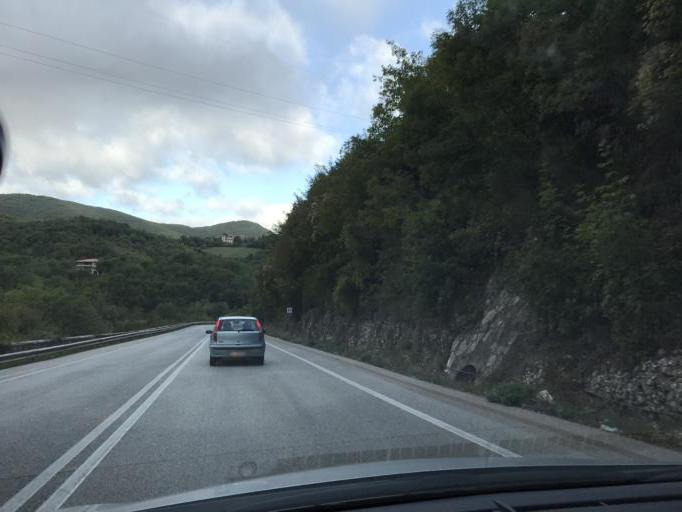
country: IT
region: Umbria
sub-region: Provincia di Terni
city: Ferentillo
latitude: 42.6695
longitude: 12.7312
